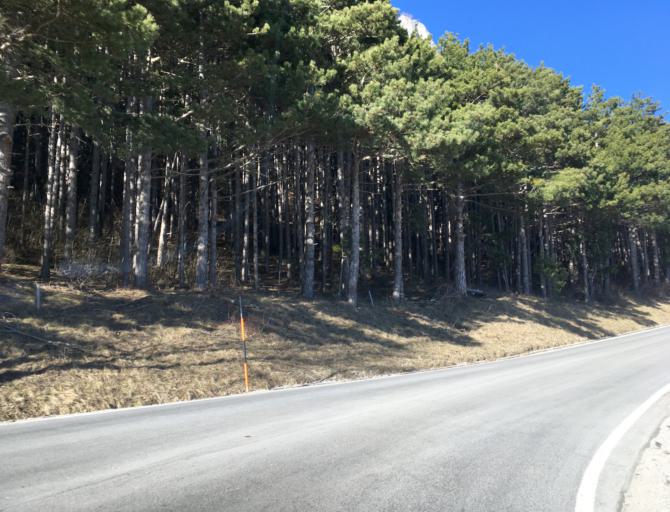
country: AT
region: Lower Austria
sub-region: Politischer Bezirk Neunkirchen
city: Willendorf am Steinfelde
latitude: 47.8280
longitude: 16.0509
